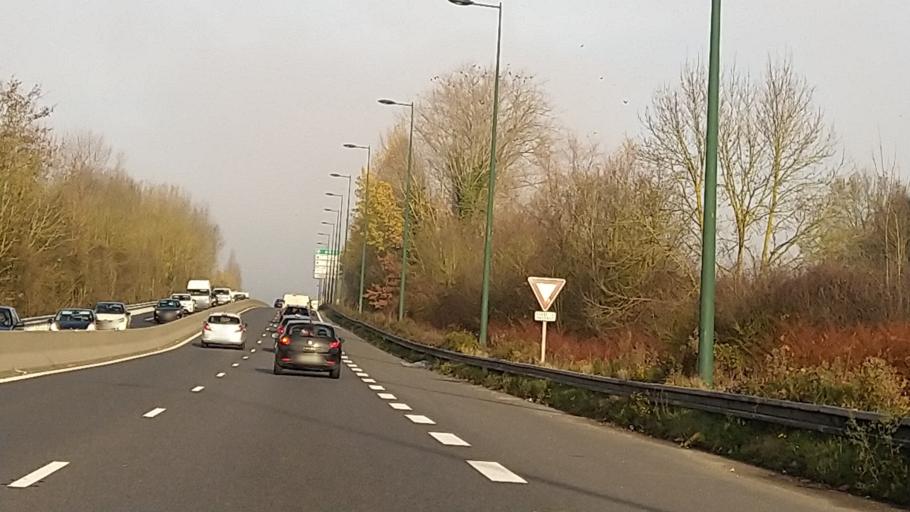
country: FR
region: Ile-de-France
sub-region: Departement du Val-d'Oise
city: Mours
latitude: 49.1357
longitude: 2.2555
